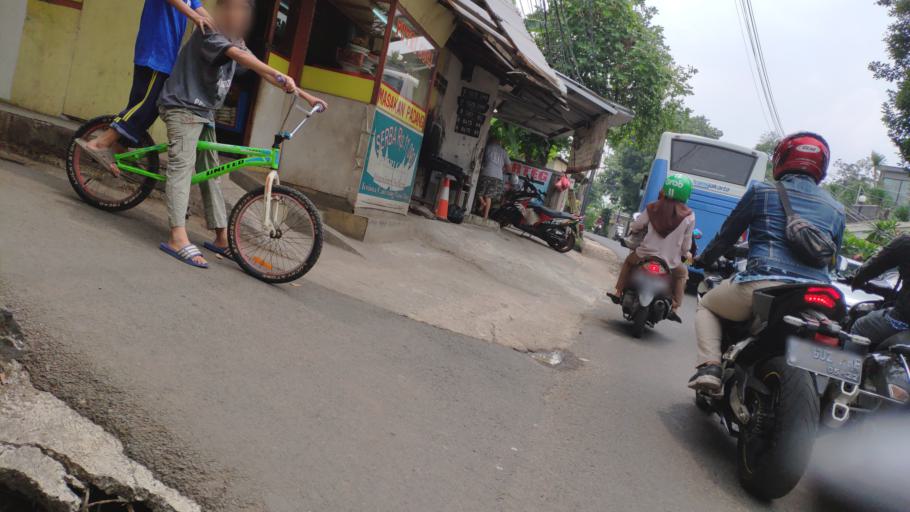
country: ID
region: West Java
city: Depok
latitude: -6.3181
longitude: 106.8343
